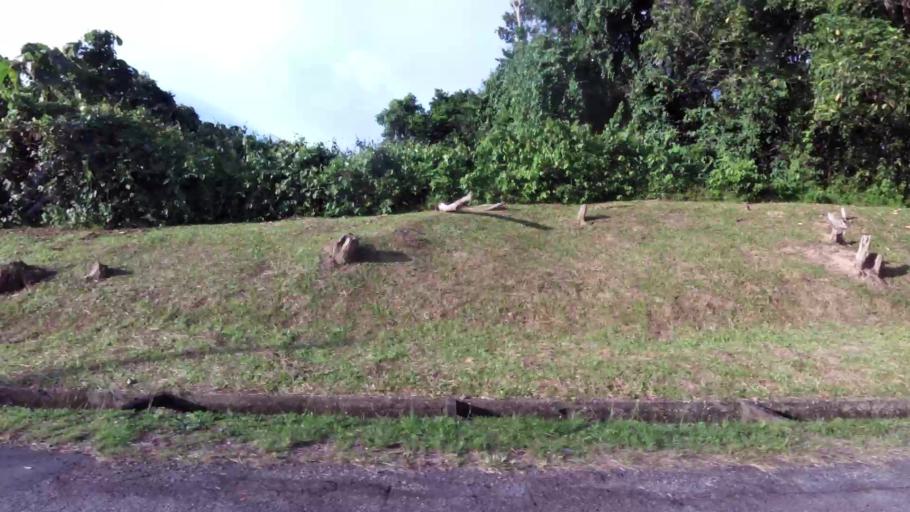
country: BN
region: Brunei and Muara
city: Bandar Seri Begawan
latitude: 4.9726
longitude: 114.9835
